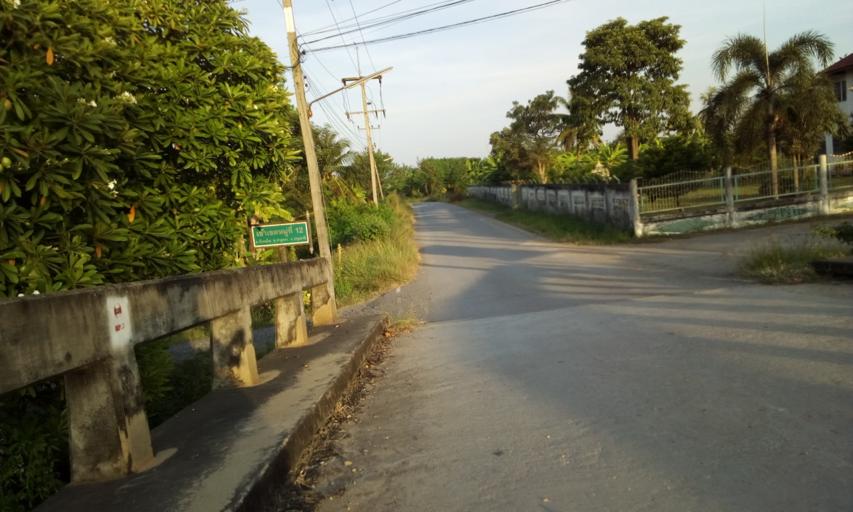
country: TH
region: Pathum Thani
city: Ban Lam Luk Ka
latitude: 14.0353
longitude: 100.8456
